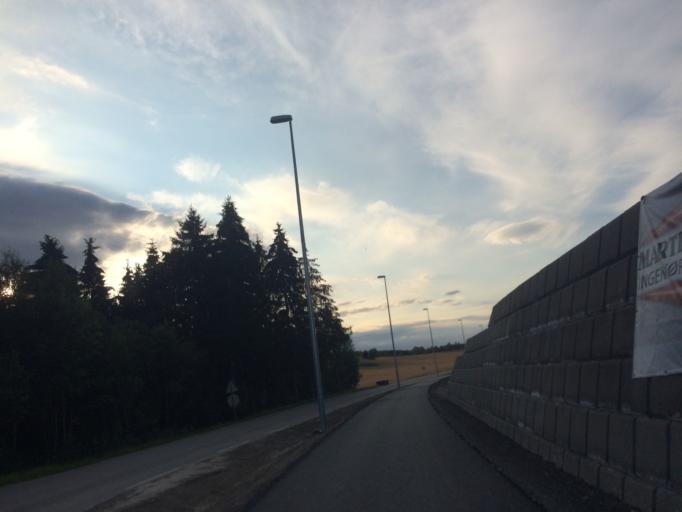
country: NO
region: Akershus
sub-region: Ski
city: Ski
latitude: 59.6852
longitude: 10.8705
